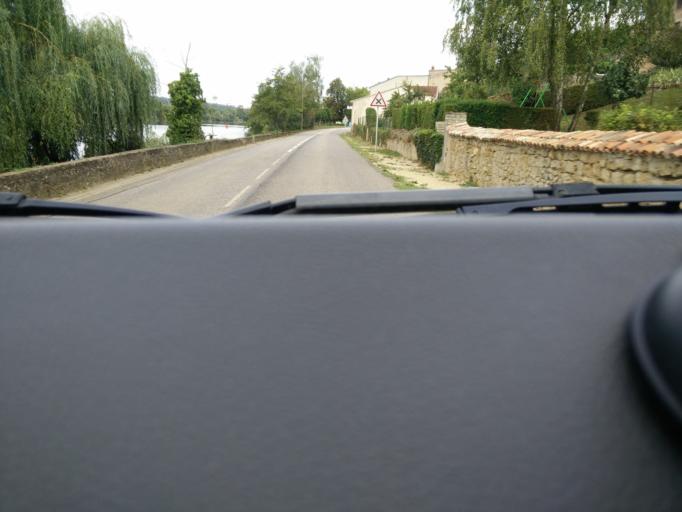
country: FR
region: Lorraine
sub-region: Departement de Meurthe-et-Moselle
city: Belleville
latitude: 48.8213
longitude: 6.1164
